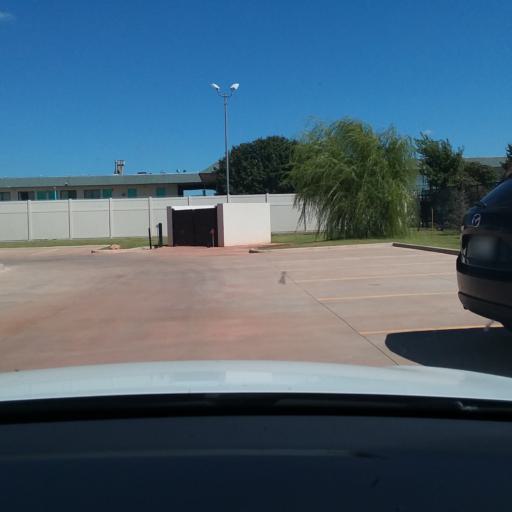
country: US
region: Oklahoma
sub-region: Oklahoma County
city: Edmond
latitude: 35.5900
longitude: -97.4334
